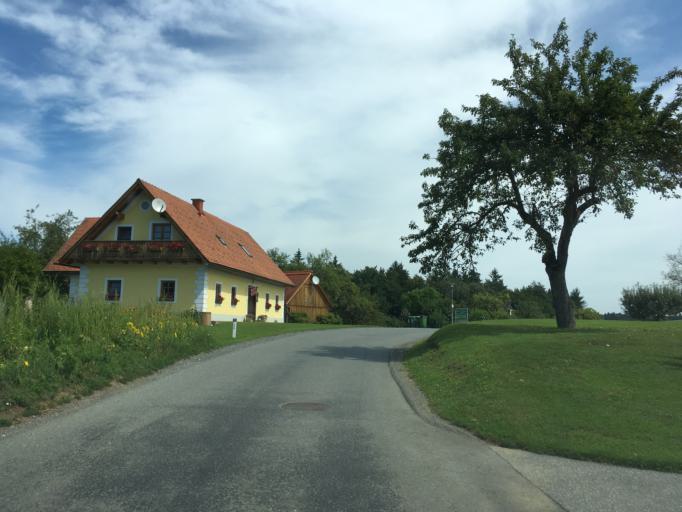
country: AT
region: Styria
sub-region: Politischer Bezirk Leibnitz
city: Pistorf
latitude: 46.7942
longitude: 15.3896
